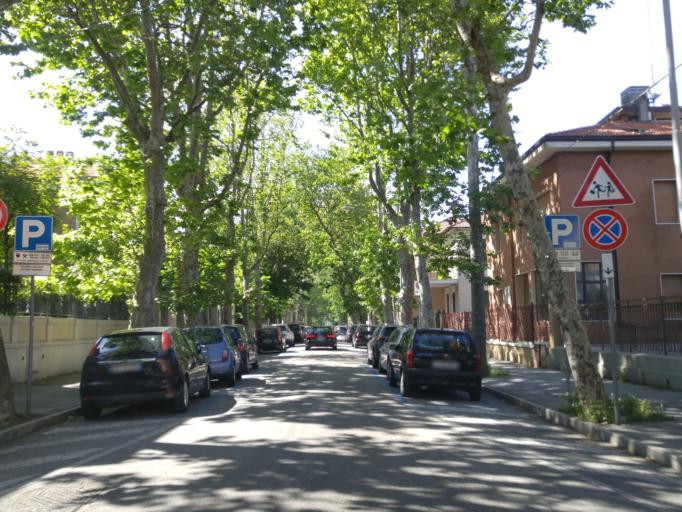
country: IT
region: The Marches
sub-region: Provincia di Pesaro e Urbino
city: Pesaro
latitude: 43.9106
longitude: 12.9194
